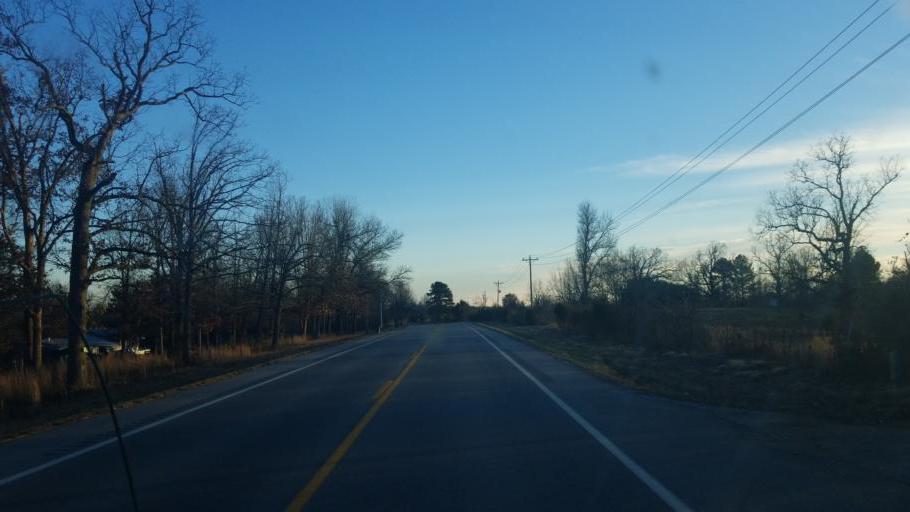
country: US
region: Arkansas
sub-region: Baxter County
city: Mountain Home
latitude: 36.3796
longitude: -92.1519
